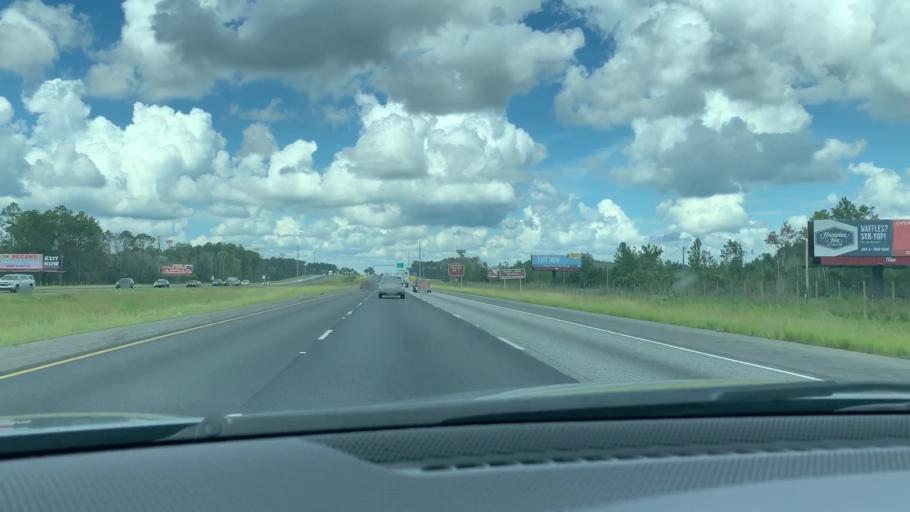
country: US
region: Georgia
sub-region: Camden County
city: Kingsland
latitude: 30.7835
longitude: -81.6572
